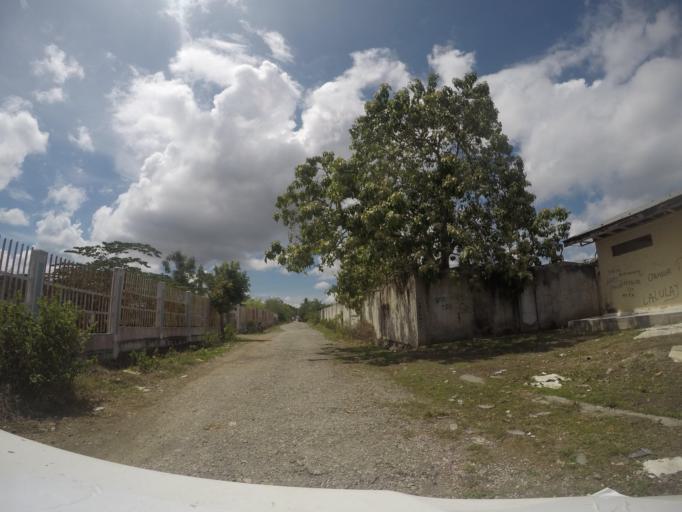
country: TL
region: Baucau
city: Baucau
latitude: -8.4713
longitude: 126.4571
